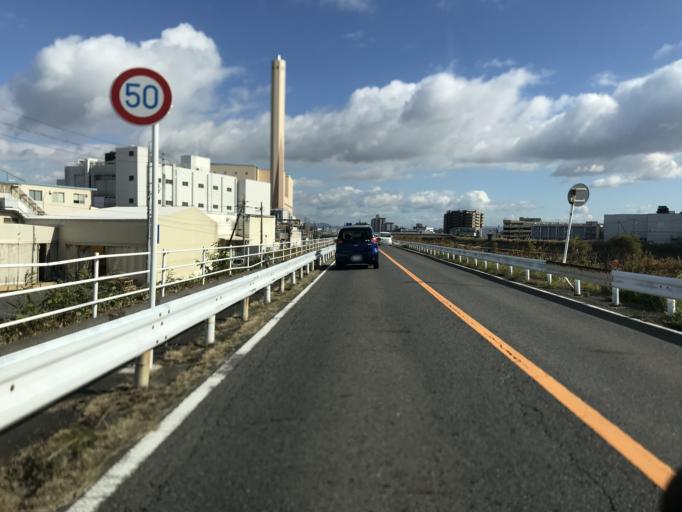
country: JP
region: Aichi
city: Nagoya-shi
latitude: 35.2276
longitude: 136.8809
